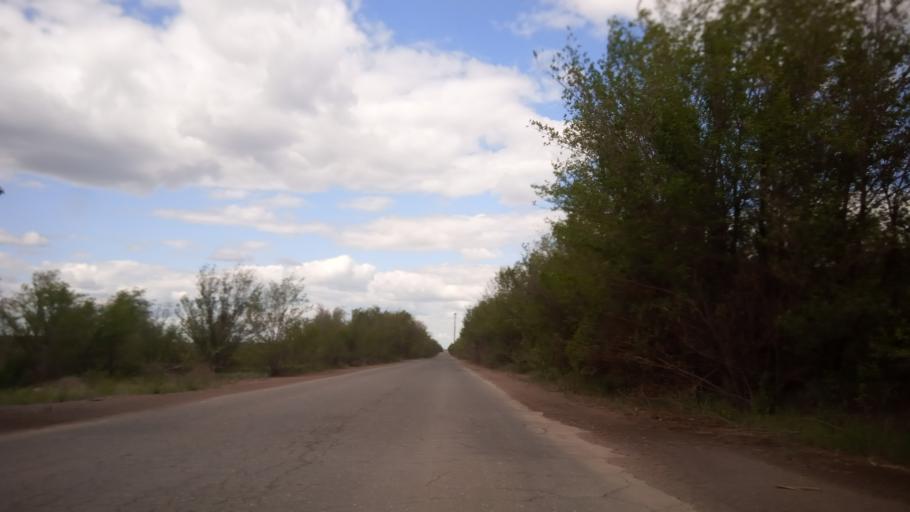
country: RU
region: Orenburg
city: Novotroitsk
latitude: 51.2436
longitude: 58.3576
